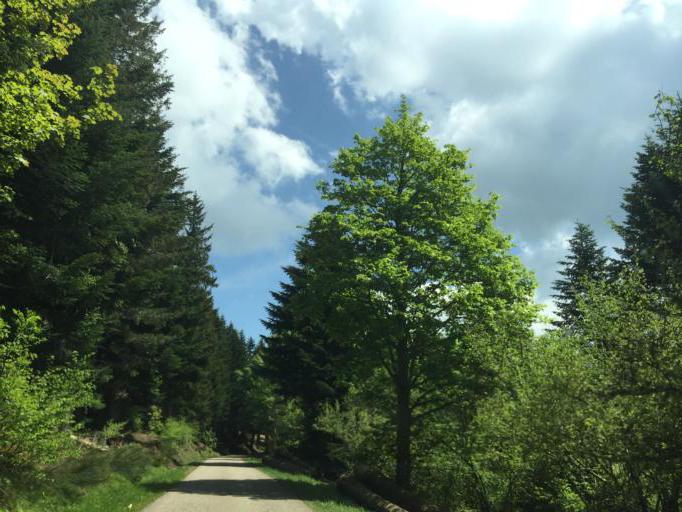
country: FR
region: Rhone-Alpes
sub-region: Departement de la Loire
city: Saint-Sauveur-en-Rue
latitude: 45.2756
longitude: 4.4526
